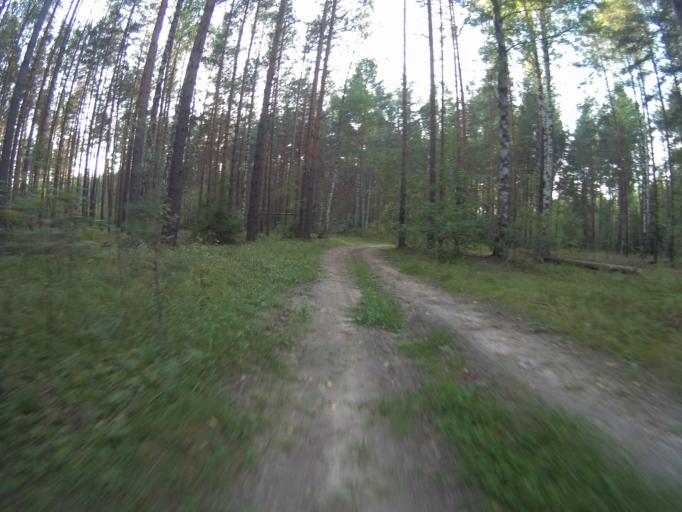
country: RU
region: Vladimir
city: Raduzhnyy
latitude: 55.9842
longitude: 40.2805
